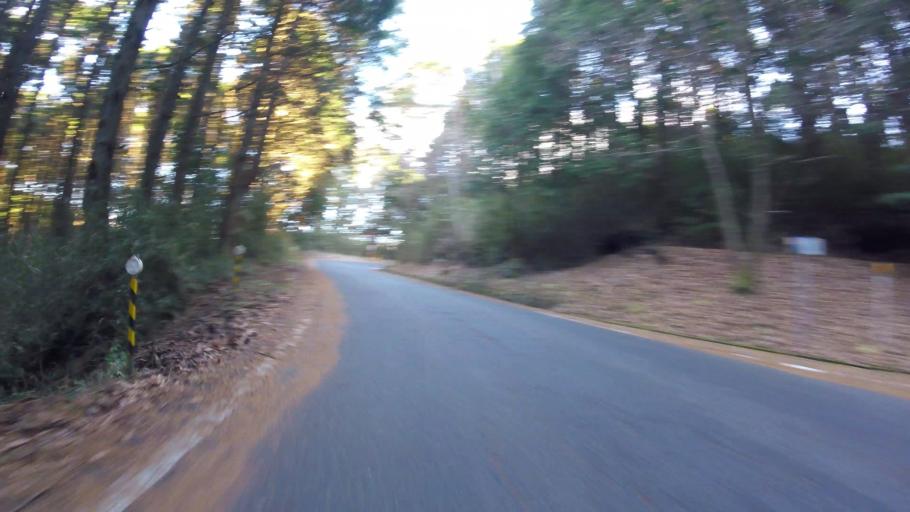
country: JP
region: Kanagawa
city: Yugawara
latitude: 35.1274
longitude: 139.0266
